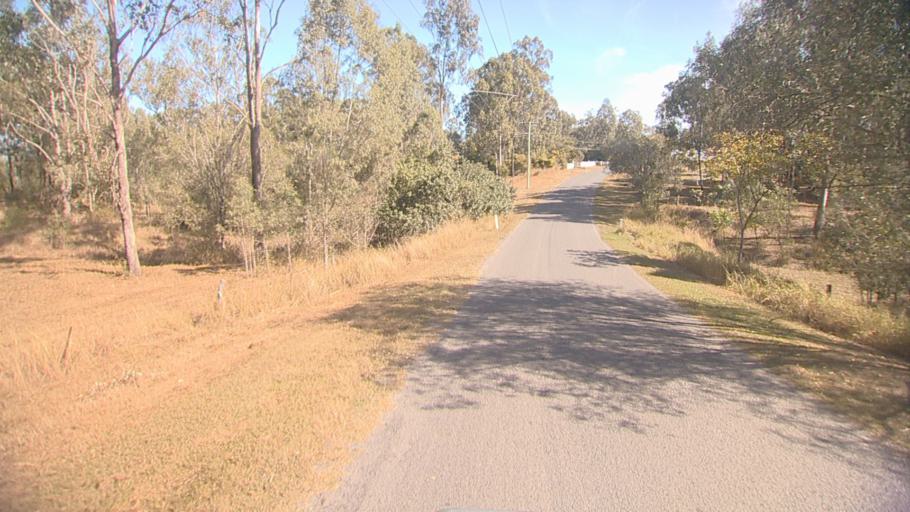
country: AU
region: Queensland
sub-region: Logan
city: Cedar Vale
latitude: -27.8739
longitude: 152.9827
